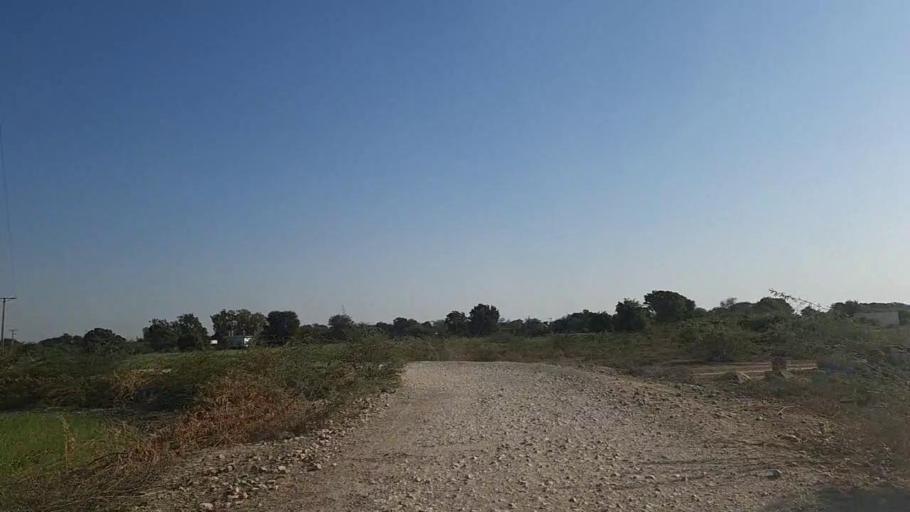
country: PK
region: Sindh
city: Naukot
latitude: 24.9493
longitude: 69.3300
